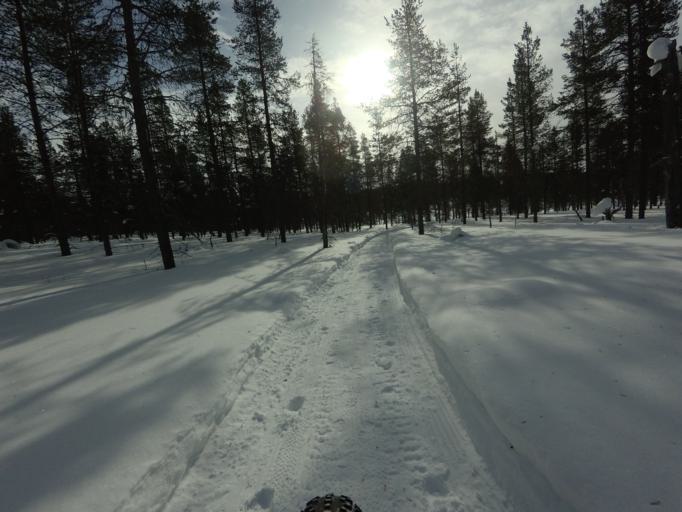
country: FI
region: Lapland
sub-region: Pohjois-Lappi
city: Ivalo
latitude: 68.3447
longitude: 27.4334
